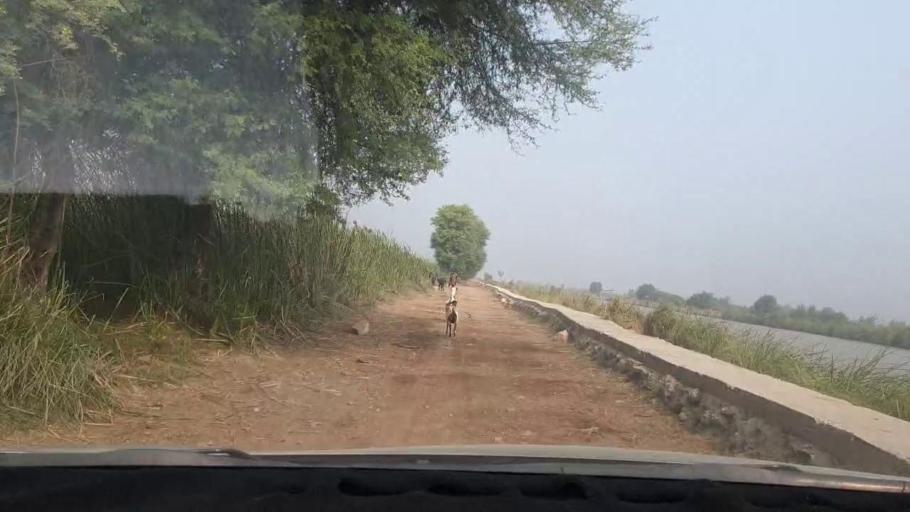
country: PK
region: Sindh
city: Matiari
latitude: 25.6600
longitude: 68.5603
